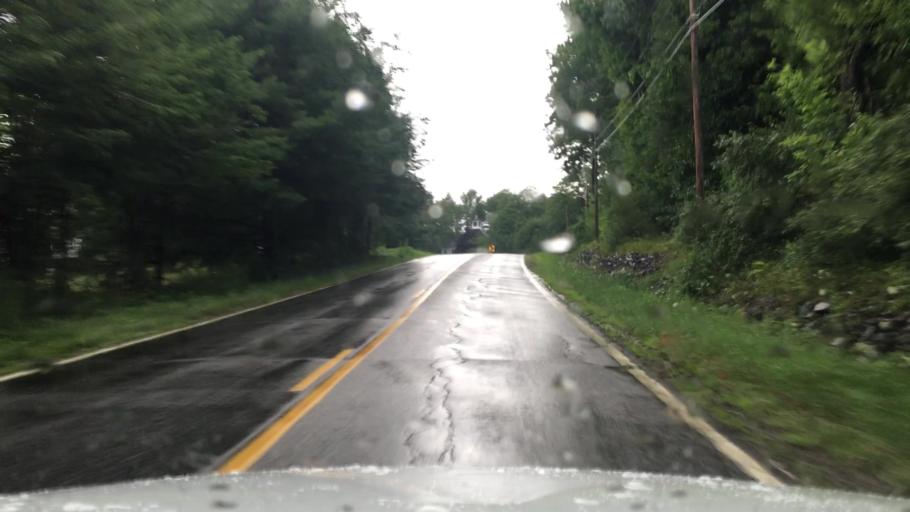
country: US
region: Maine
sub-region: Kennebec County
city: Winthrop
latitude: 44.2907
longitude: -69.9301
